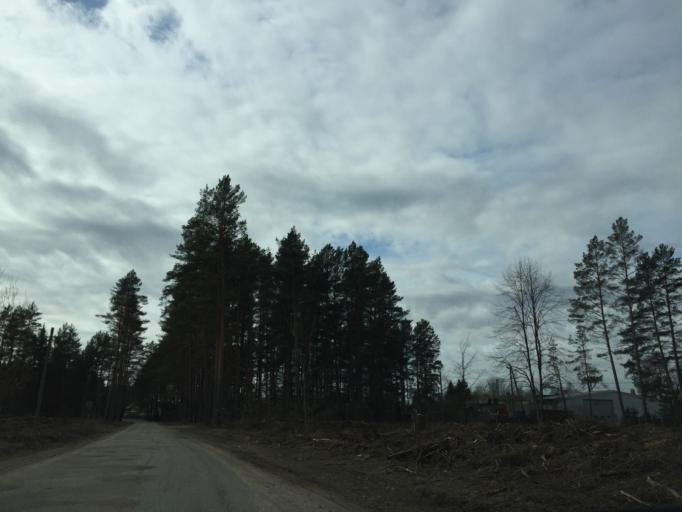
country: LV
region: Garkalne
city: Garkalne
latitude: 57.0714
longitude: 24.4241
